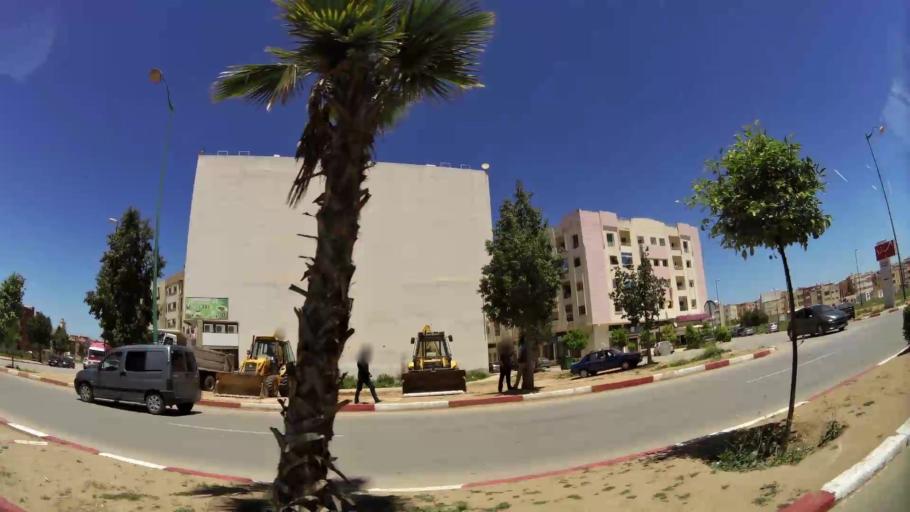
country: MA
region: Meknes-Tafilalet
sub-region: Meknes
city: Meknes
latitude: 33.8593
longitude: -5.5685
